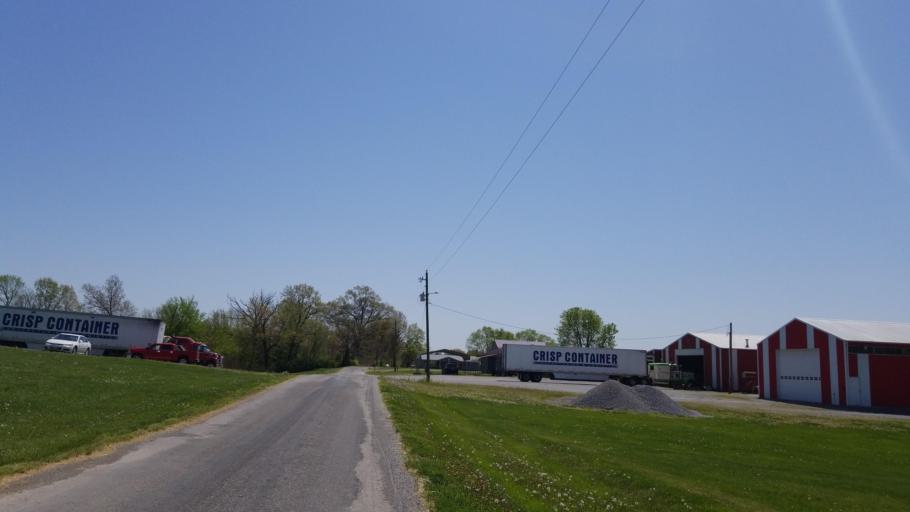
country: US
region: Illinois
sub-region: Saline County
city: Harrisburg
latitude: 37.8486
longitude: -88.6010
